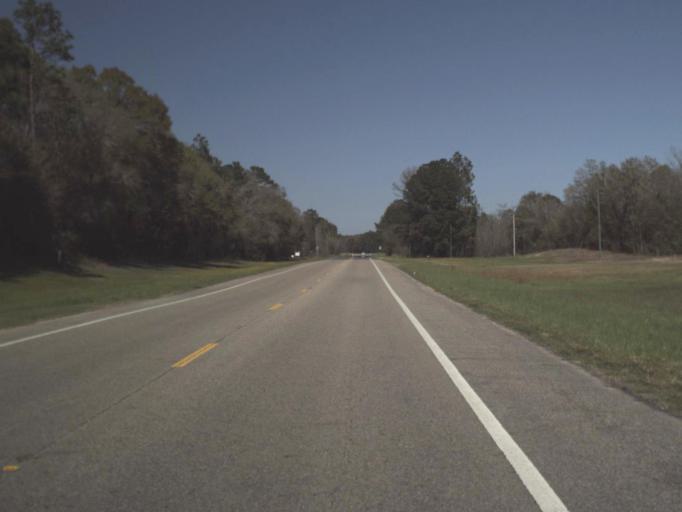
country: US
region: Florida
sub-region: Walton County
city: DeFuniak Springs
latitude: 30.7391
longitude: -85.9082
